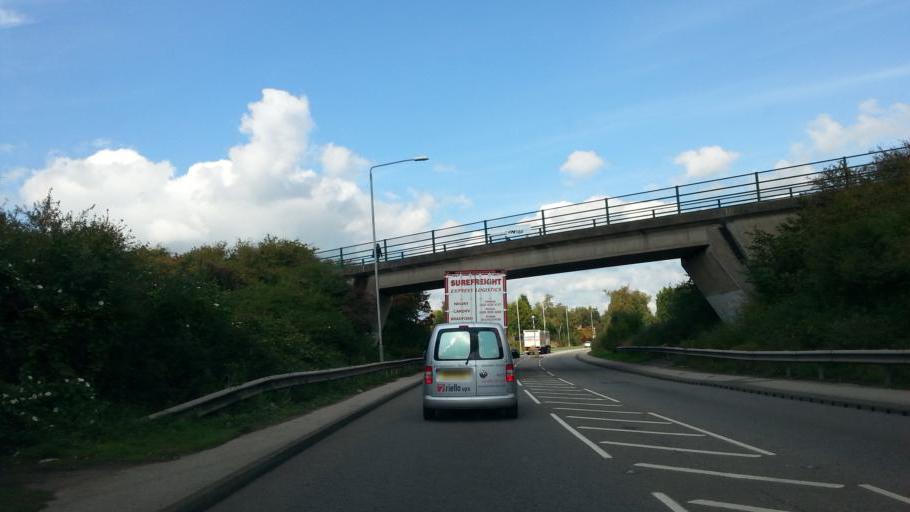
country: GB
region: England
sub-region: Nottinghamshire
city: Sutton in Ashfield
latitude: 53.1165
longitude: -1.2554
